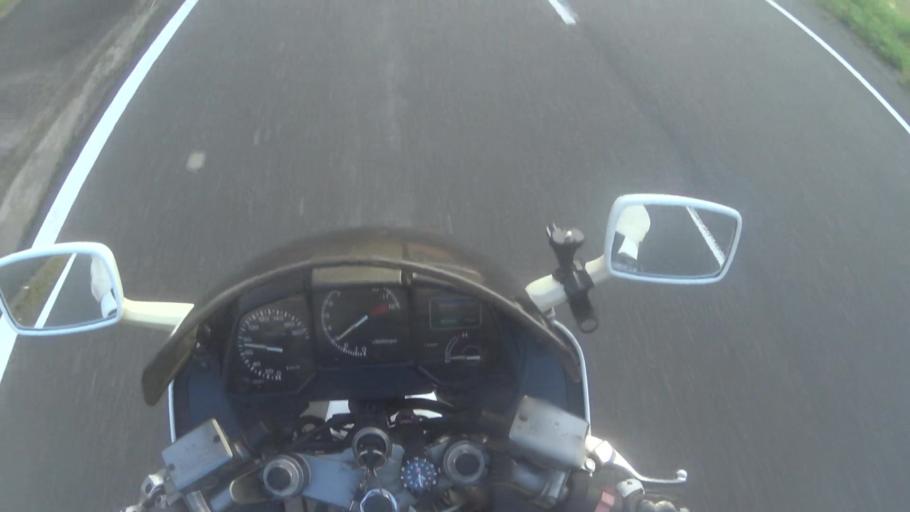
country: JP
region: Kyoto
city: Miyazu
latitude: 35.5586
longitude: 135.0817
